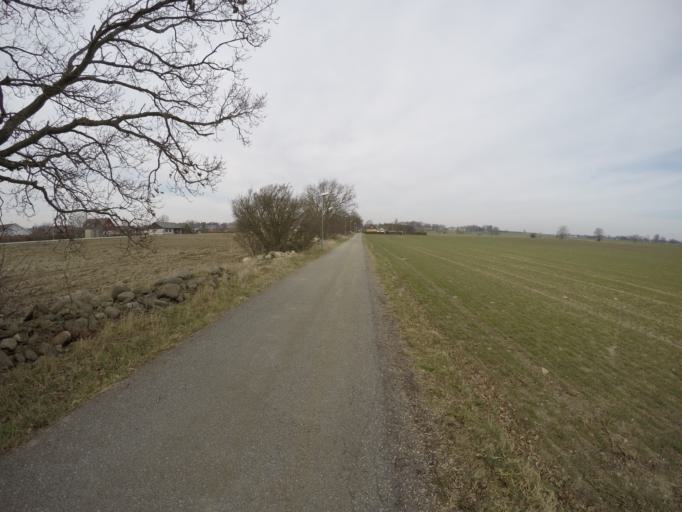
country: SE
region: Skane
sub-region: Ystads Kommun
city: Kopingebro
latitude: 55.4328
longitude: 14.1145
